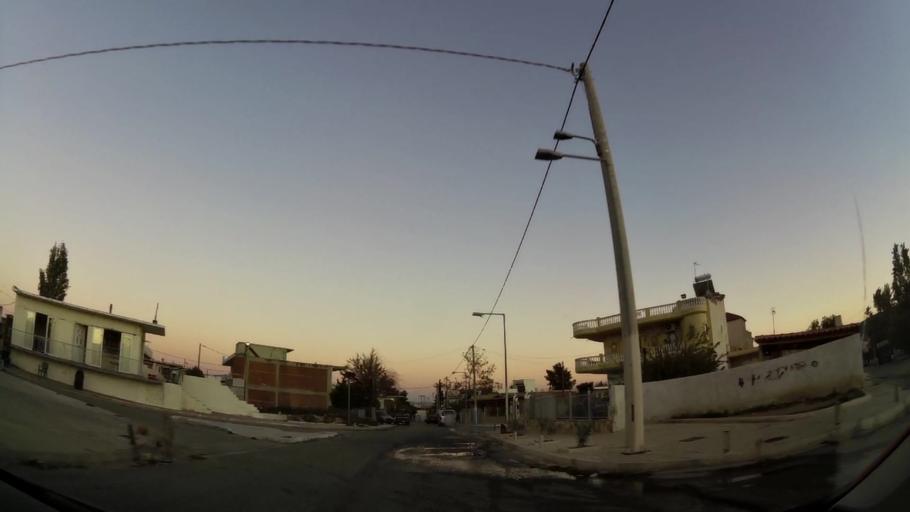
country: GR
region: Attica
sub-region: Nomarchia Dytikis Attikis
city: Ano Liosia
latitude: 38.0811
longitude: 23.6946
